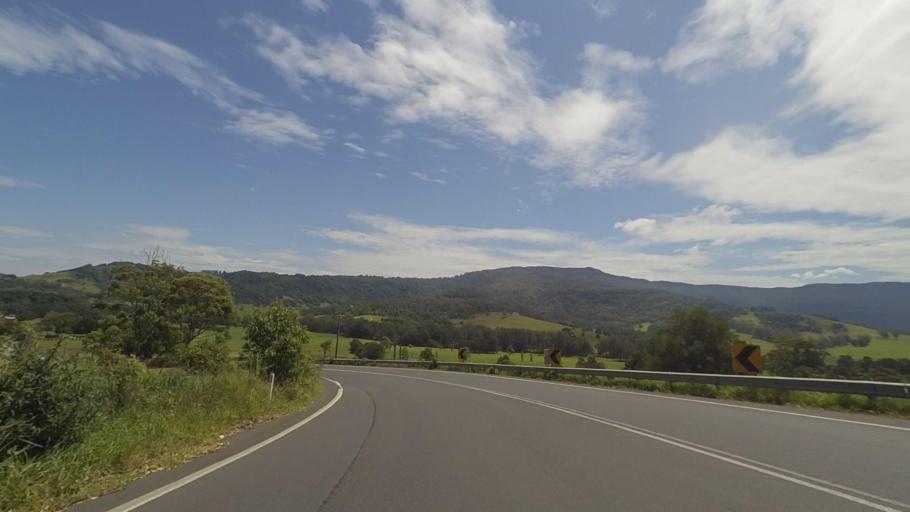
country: AU
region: New South Wales
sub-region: Kiama
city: Gerringong
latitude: -34.7390
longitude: 150.7678
